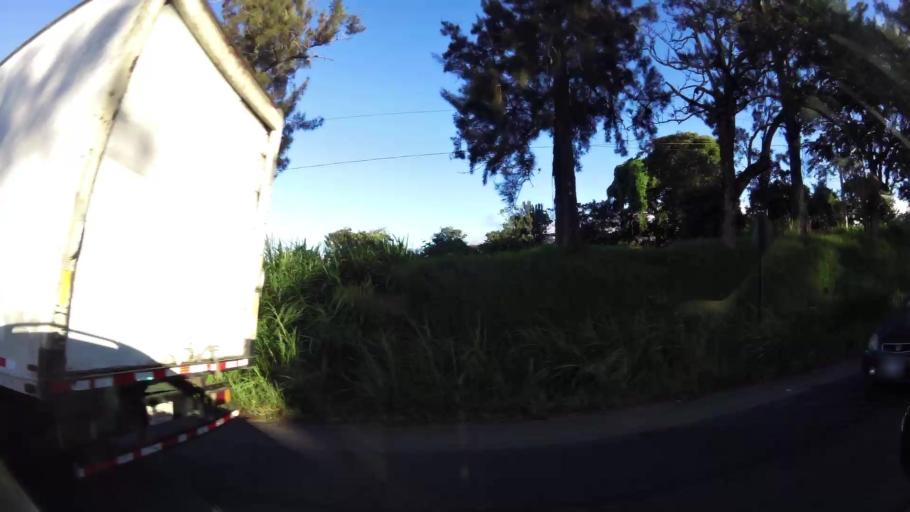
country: CR
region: Heredia
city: Angeles
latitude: 9.9795
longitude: -84.0508
